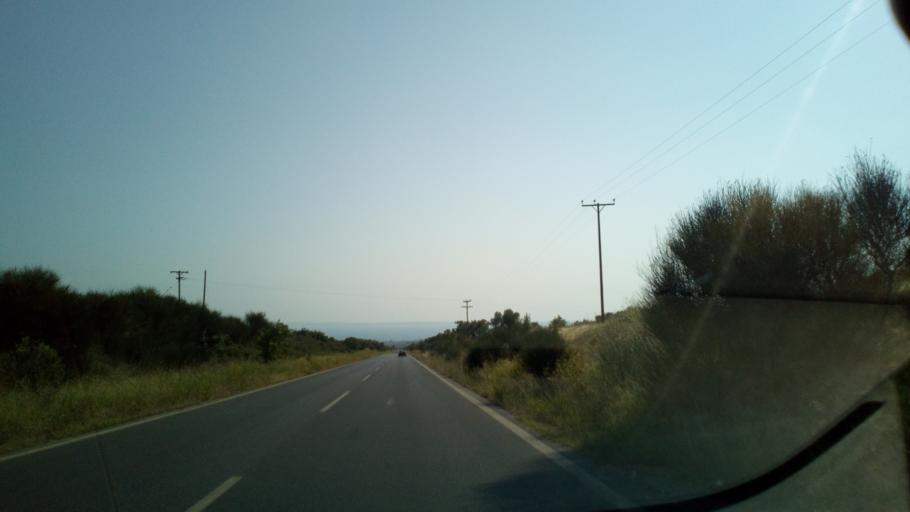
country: GR
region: Central Macedonia
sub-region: Nomos Chalkidikis
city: Kalyves Polygyrou
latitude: 40.3099
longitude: 23.4397
